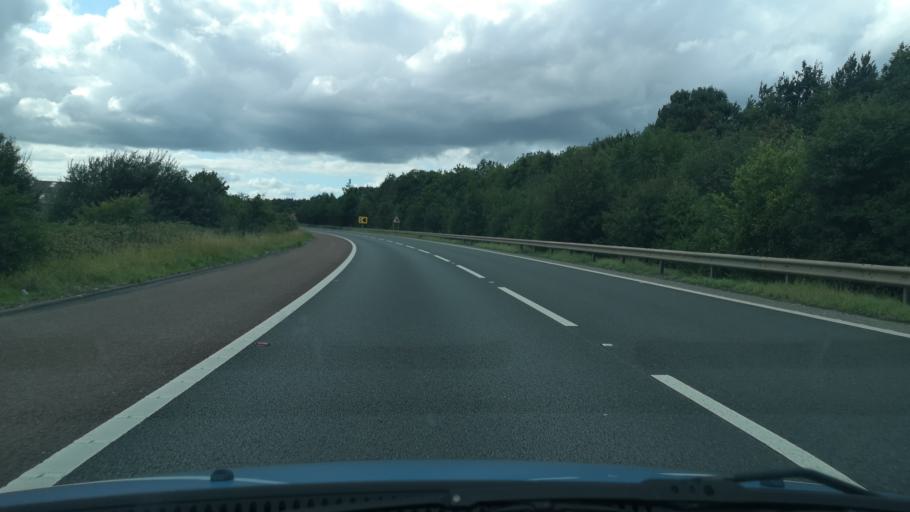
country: GB
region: England
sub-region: East Riding of Yorkshire
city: Rawcliffe
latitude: 53.6822
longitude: -0.9712
